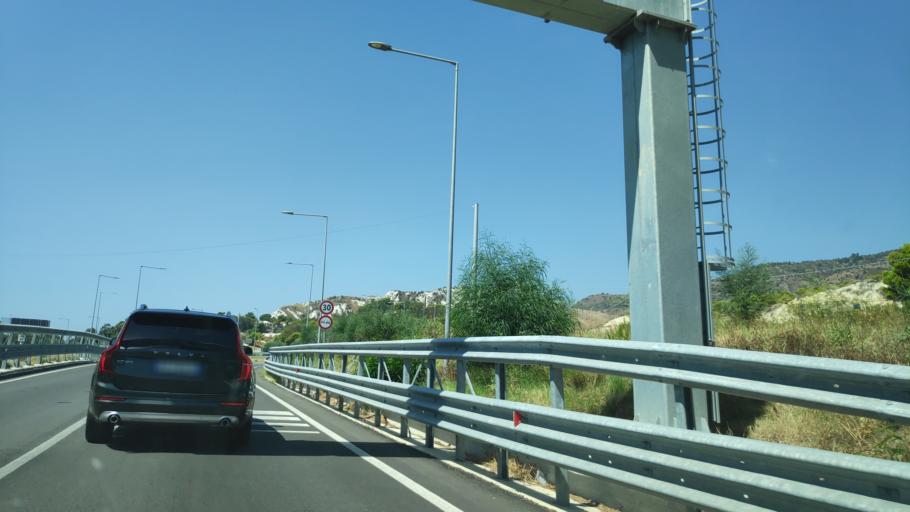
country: IT
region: Calabria
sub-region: Provincia di Reggio Calabria
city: Palizzi Marina
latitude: 37.9221
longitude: 16.0142
